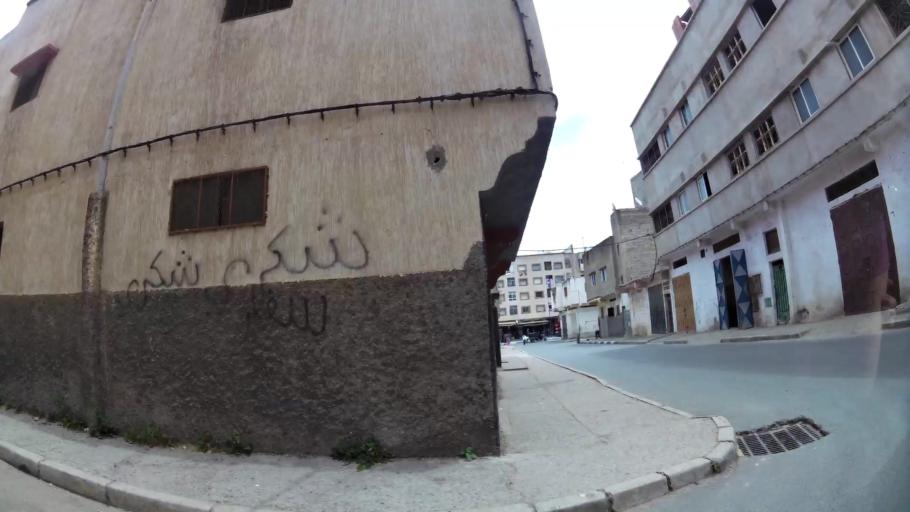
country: MA
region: Rabat-Sale-Zemmour-Zaer
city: Sale
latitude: 34.0584
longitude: -6.7799
